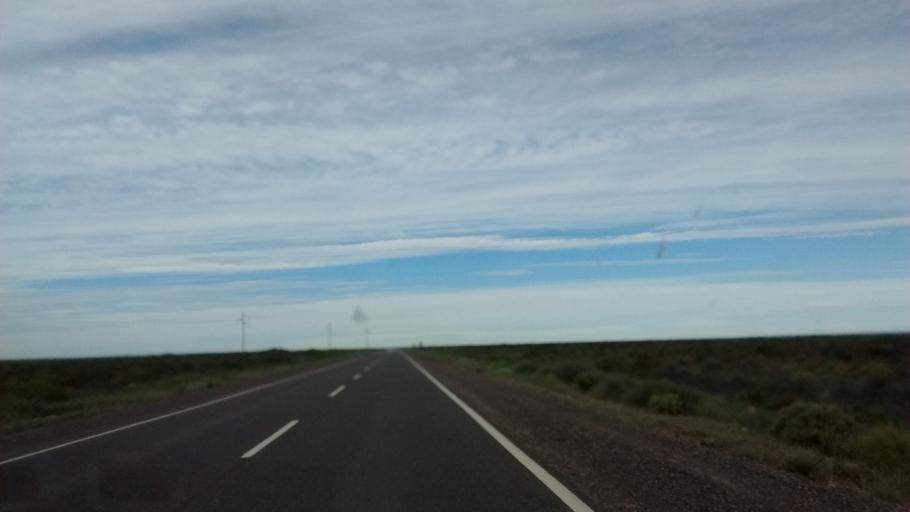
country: AR
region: Rio Negro
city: Contraalmirante Cordero
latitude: -38.6385
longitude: -68.1323
